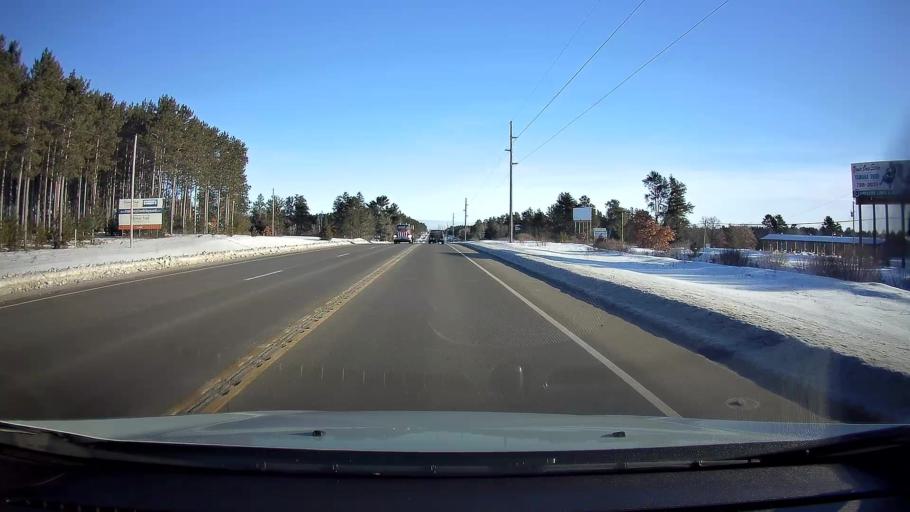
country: US
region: Wisconsin
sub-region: Sawyer County
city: Hayward
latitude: 45.9916
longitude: -91.5177
